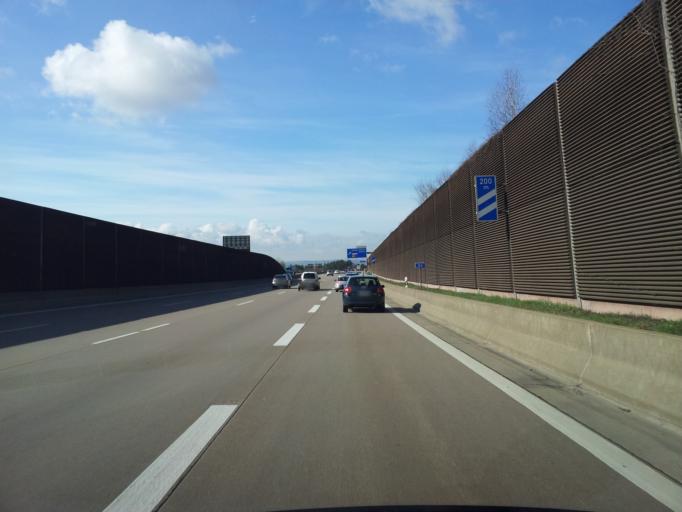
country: DE
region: Saxony
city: Albertstadt
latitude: 51.1090
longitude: 13.7373
